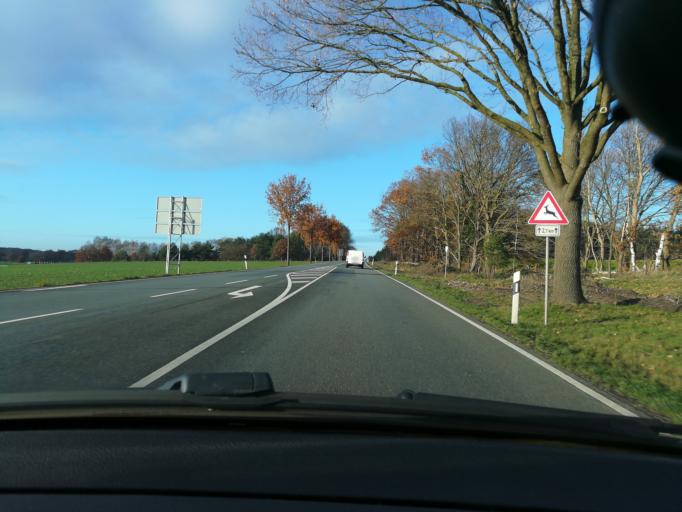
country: DE
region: Lower Saxony
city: Uchte
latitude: 52.5294
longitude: 8.8829
